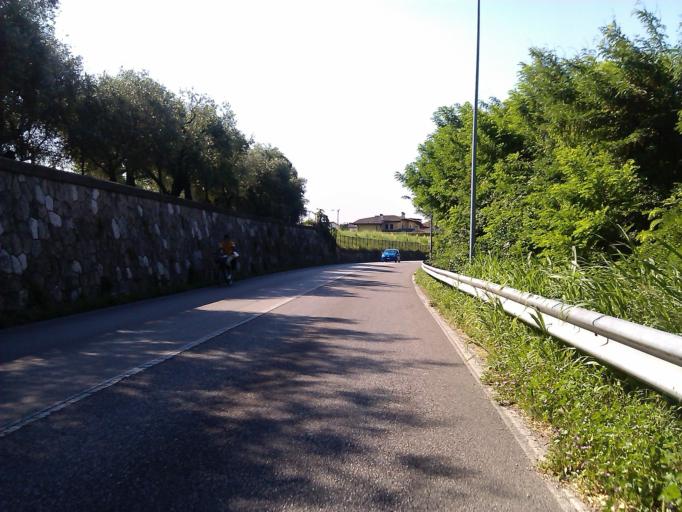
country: IT
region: Veneto
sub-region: Provincia di Vicenza
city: Bassano del Grappa
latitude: 45.7787
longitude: 11.7417
